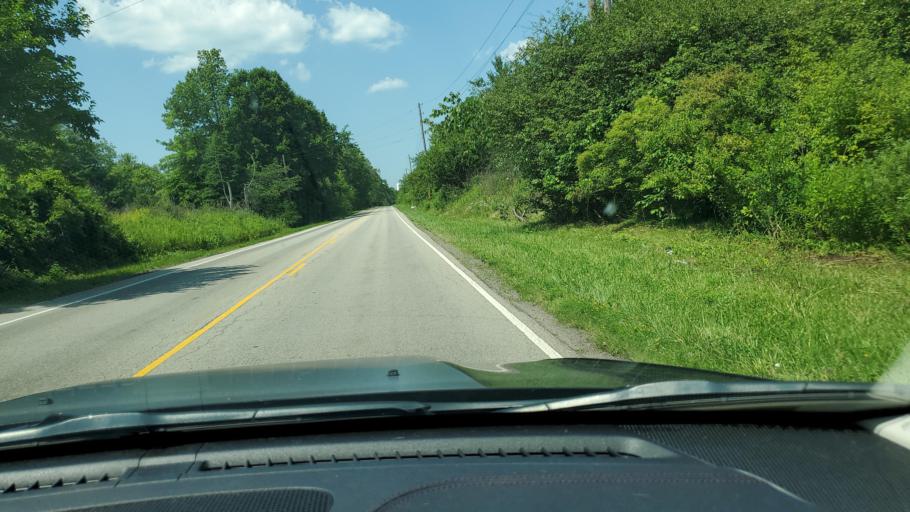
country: US
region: Ohio
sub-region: Trumbull County
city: Bolindale
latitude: 41.2054
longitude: -80.8002
